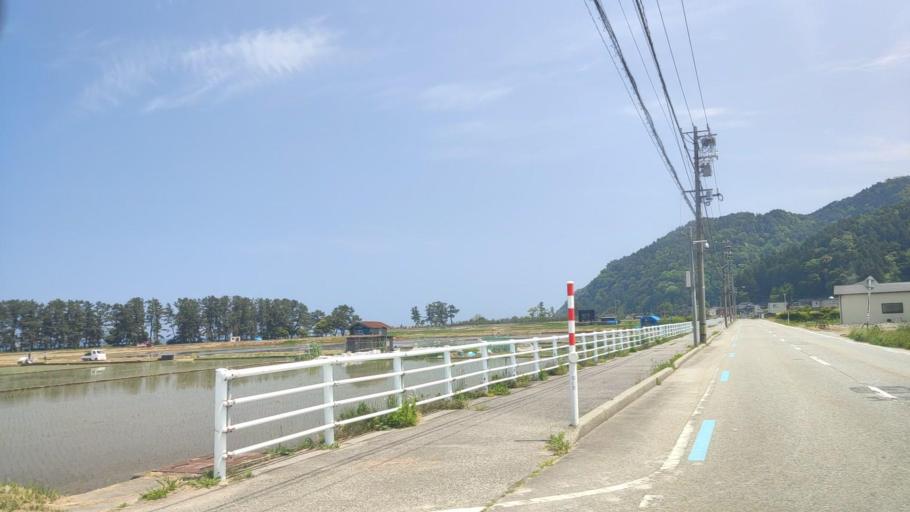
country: JP
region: Toyama
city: Nyuzen
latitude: 36.9601
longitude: 137.5682
